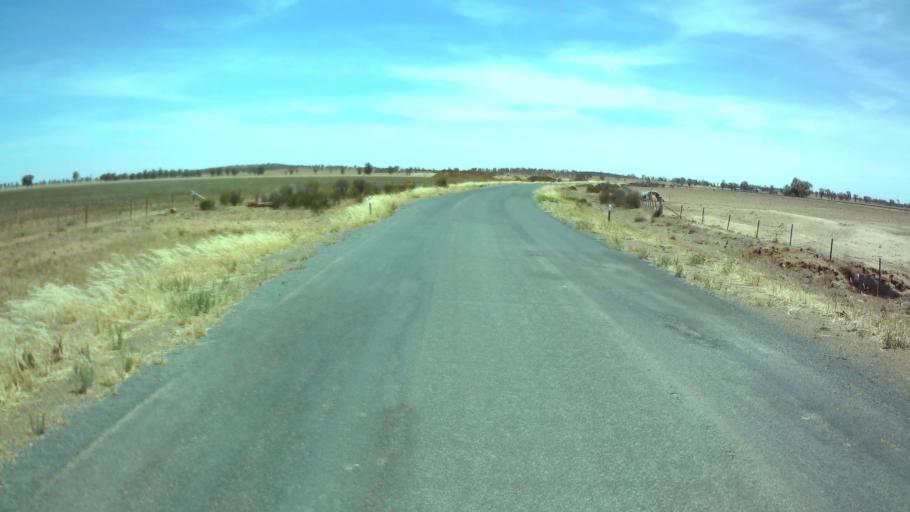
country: AU
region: New South Wales
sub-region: Weddin
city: Grenfell
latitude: -33.7512
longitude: 147.7666
